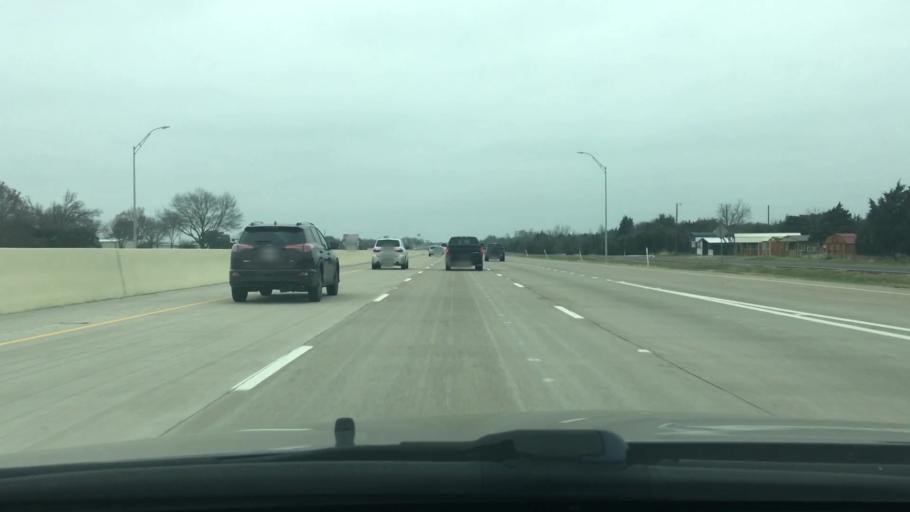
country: US
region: Texas
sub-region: Navarro County
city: Corsicana
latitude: 32.0055
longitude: -96.4327
